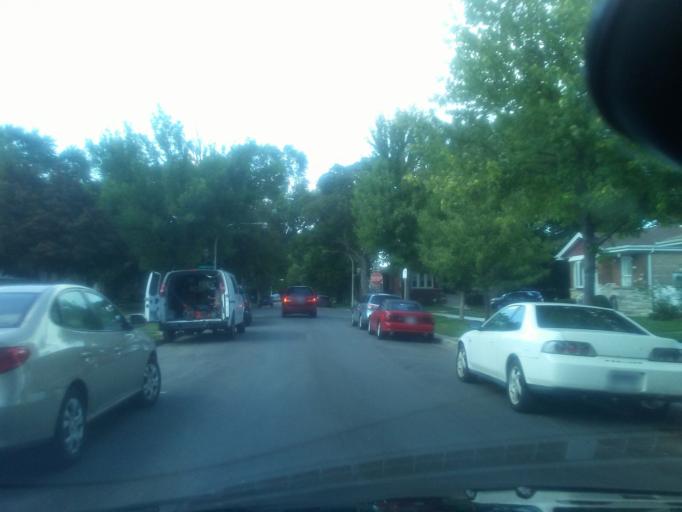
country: US
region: Illinois
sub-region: Cook County
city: Lincolnwood
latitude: 41.9715
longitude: -87.7330
